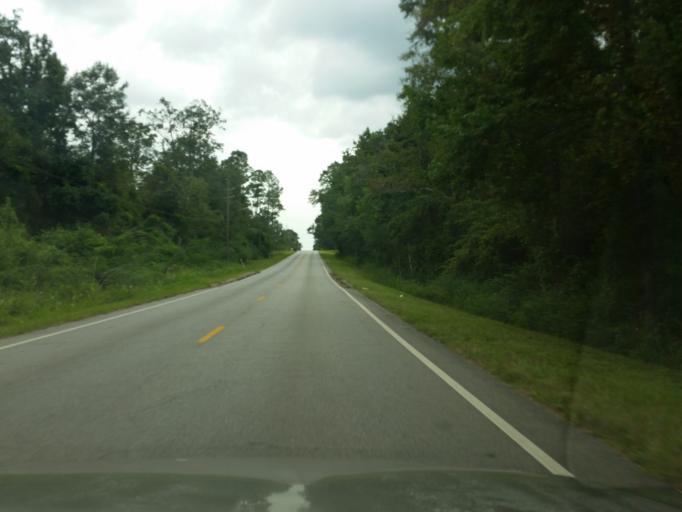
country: US
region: Florida
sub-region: Escambia County
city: Molino
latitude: 30.7072
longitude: -87.3349
